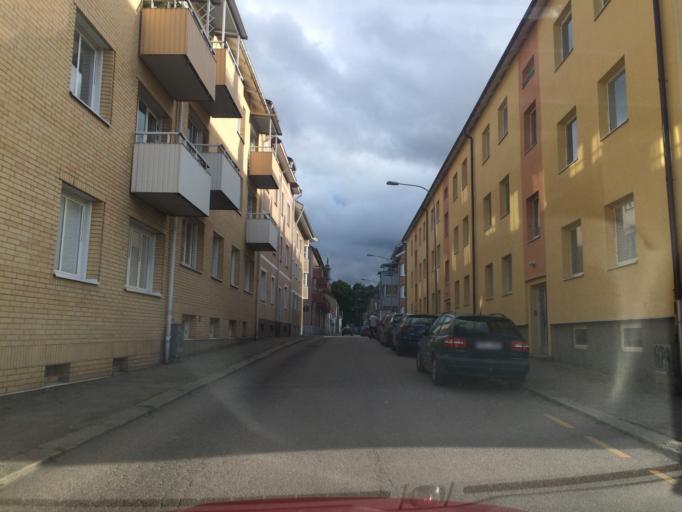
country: SE
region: Vaestra Goetaland
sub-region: Vanersborgs Kommun
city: Vanersborg
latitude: 58.3835
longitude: 12.3276
